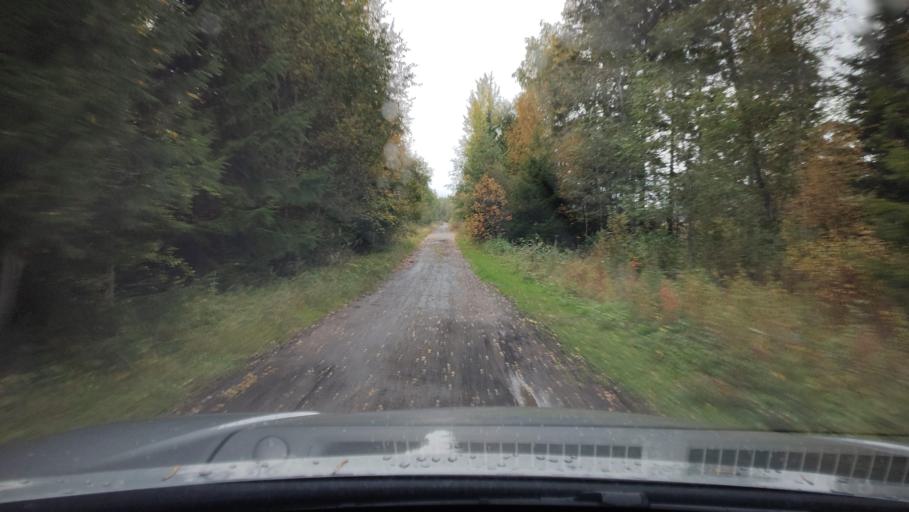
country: FI
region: Ostrobothnia
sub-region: Sydosterbotten
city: Kristinestad
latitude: 62.2665
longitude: 21.4605
